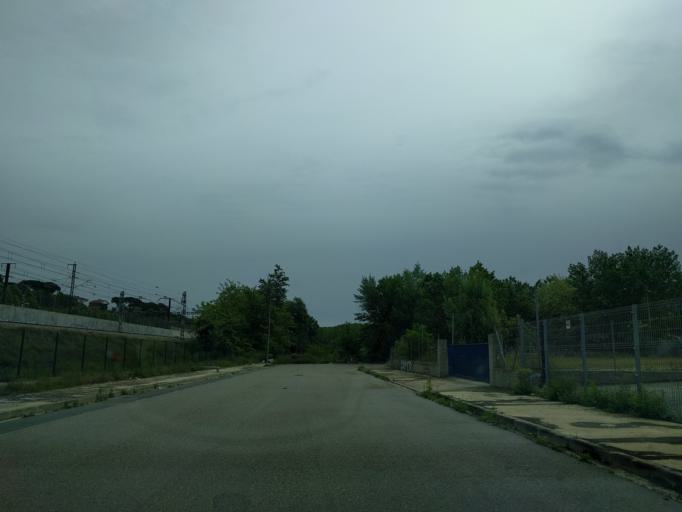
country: ES
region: Catalonia
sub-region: Provincia de Girona
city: Breda
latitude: 41.7302
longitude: 2.5840
